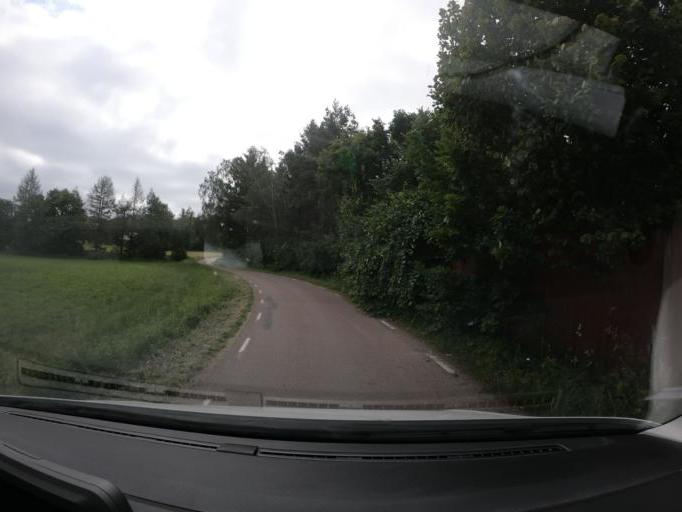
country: SE
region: Skane
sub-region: Klippans Kommun
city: Ljungbyhed
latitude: 56.0451
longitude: 13.3229
